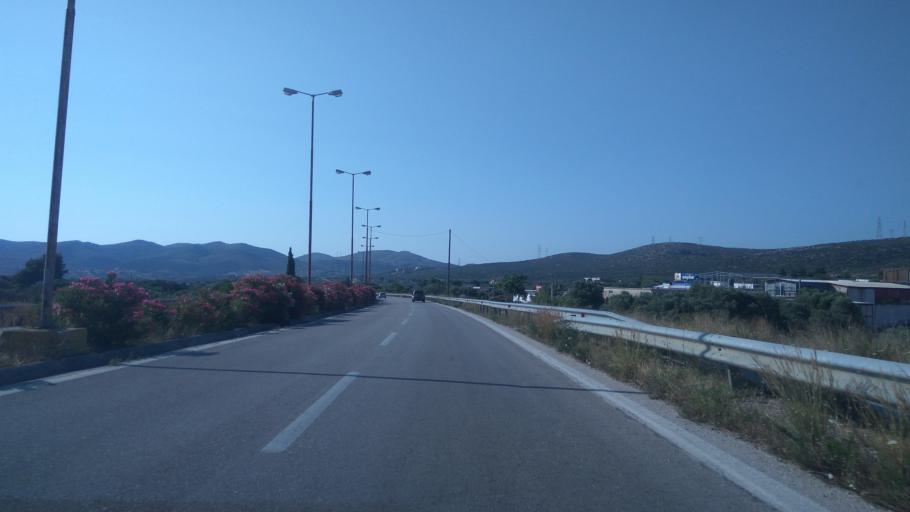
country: GR
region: Attica
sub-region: Nomarchia Anatolikis Attikis
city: Keratea
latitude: 37.8055
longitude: 23.9909
